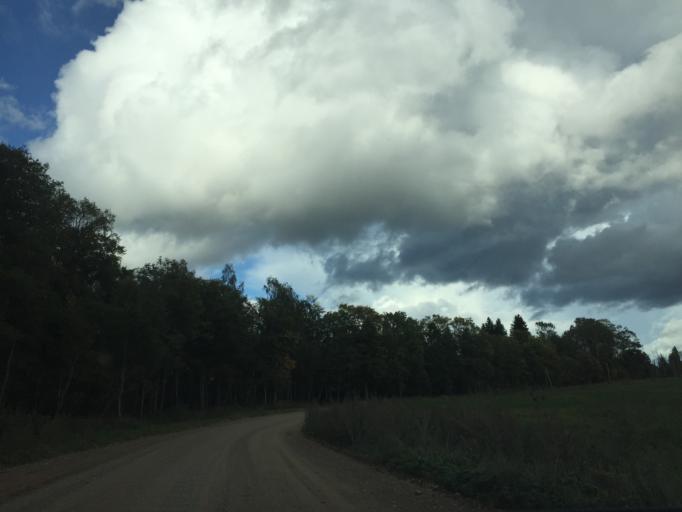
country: LV
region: Malpils
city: Malpils
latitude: 57.0591
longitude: 25.1423
